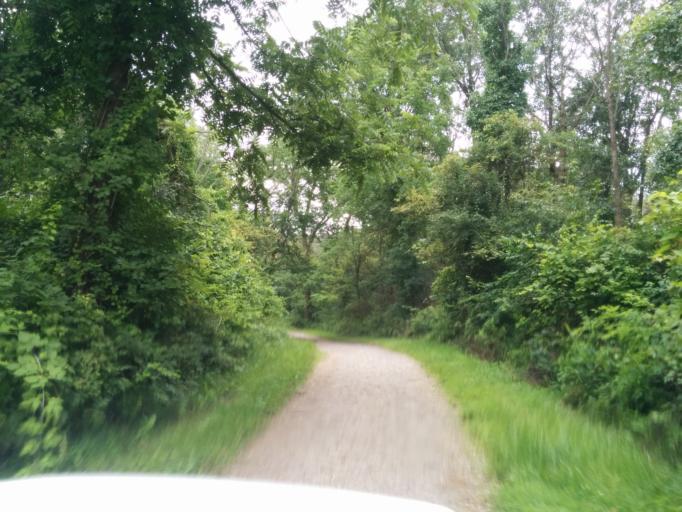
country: US
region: Illinois
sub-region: Cook County
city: Willow Springs
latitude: 41.7038
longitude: -87.8899
